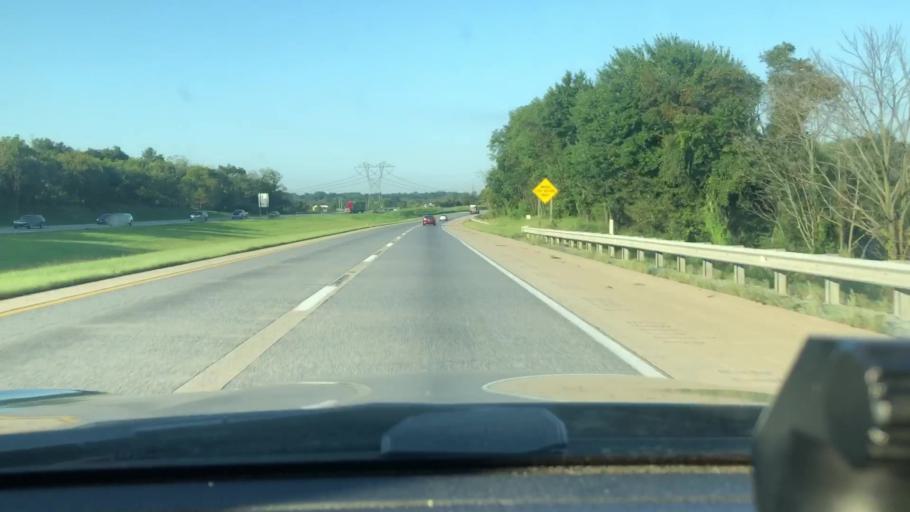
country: US
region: Pennsylvania
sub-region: Lebanon County
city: Palmyra
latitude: 40.4013
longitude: -76.6102
